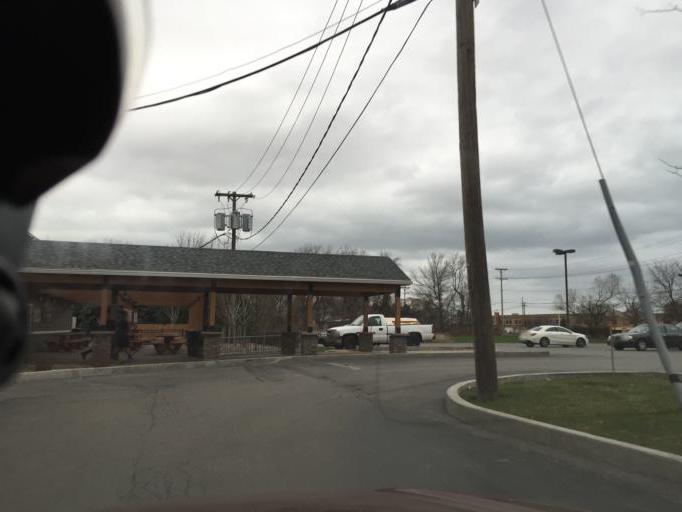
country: US
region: New York
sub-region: Monroe County
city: Greece
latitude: 43.2536
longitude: -77.6663
